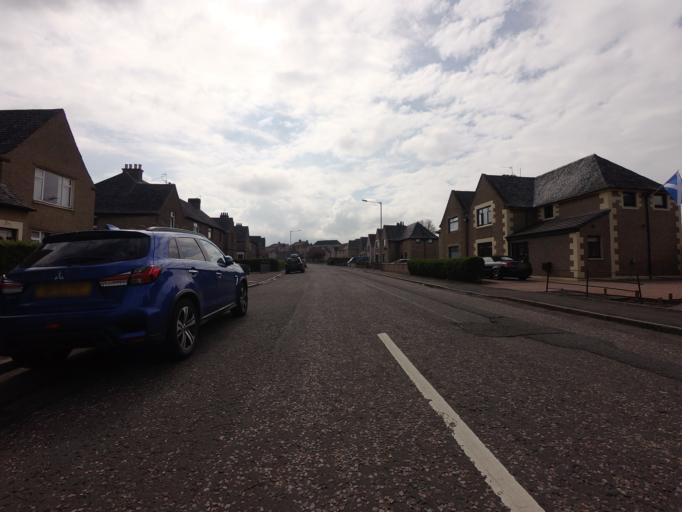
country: GB
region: Scotland
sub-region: Falkirk
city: Falkirk
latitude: 56.0028
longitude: -3.7702
